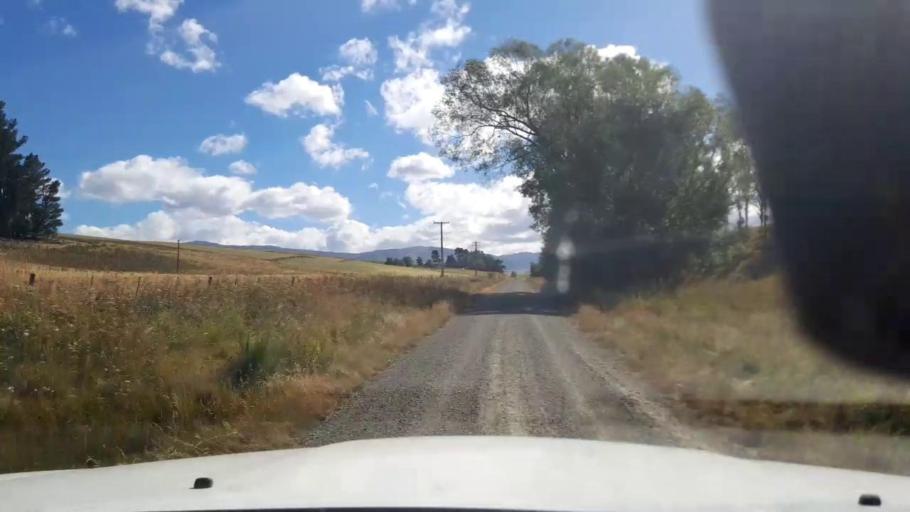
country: NZ
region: Canterbury
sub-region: Timaru District
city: Pleasant Point
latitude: -44.2387
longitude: 170.8647
